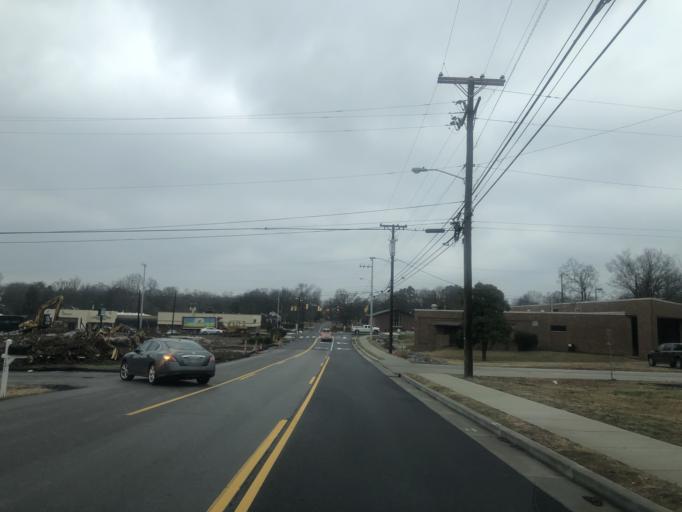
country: US
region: Tennessee
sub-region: Davidson County
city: Lakewood
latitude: 36.1704
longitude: -86.6826
